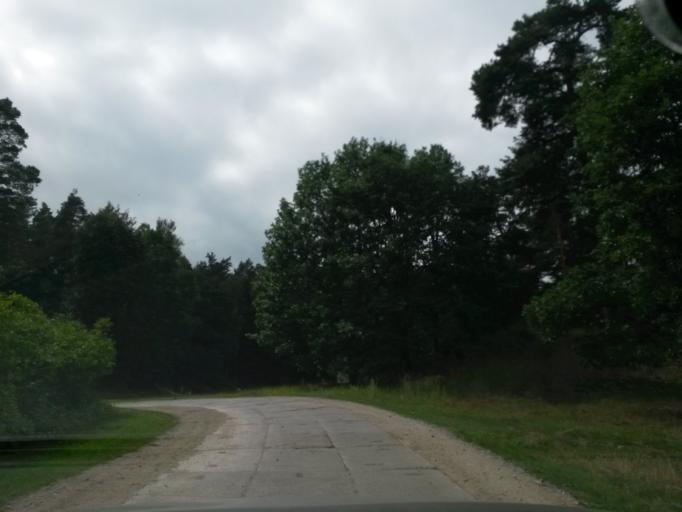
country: DE
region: Brandenburg
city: Gerswalde
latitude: 53.0933
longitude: 13.8419
